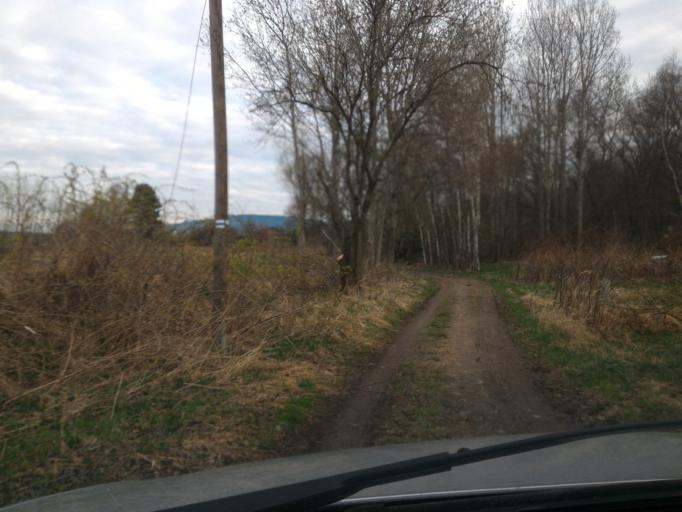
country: DE
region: Saxony
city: Eibau
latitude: 50.9655
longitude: 14.6710
